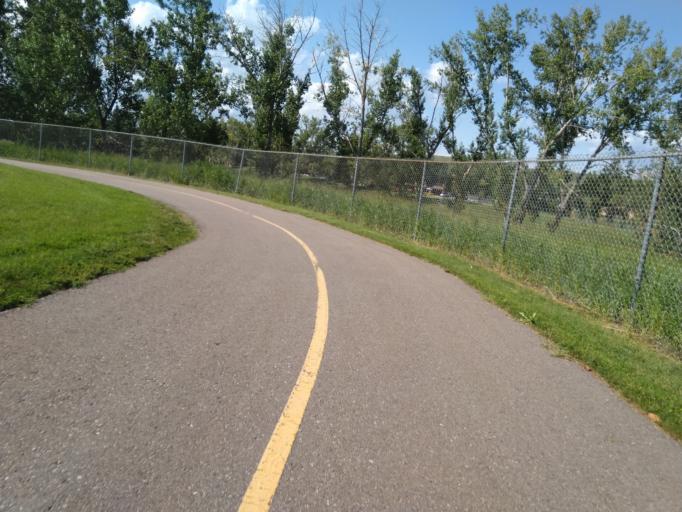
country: CA
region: Alberta
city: Calgary
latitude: 51.0784
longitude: -114.1043
